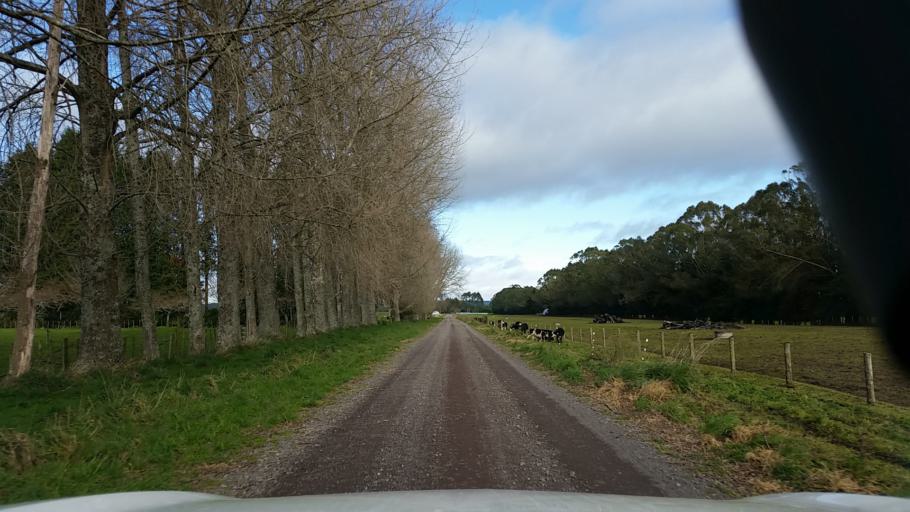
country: NZ
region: Bay of Plenty
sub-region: Whakatane District
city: Murupara
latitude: -38.4697
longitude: 176.4172
